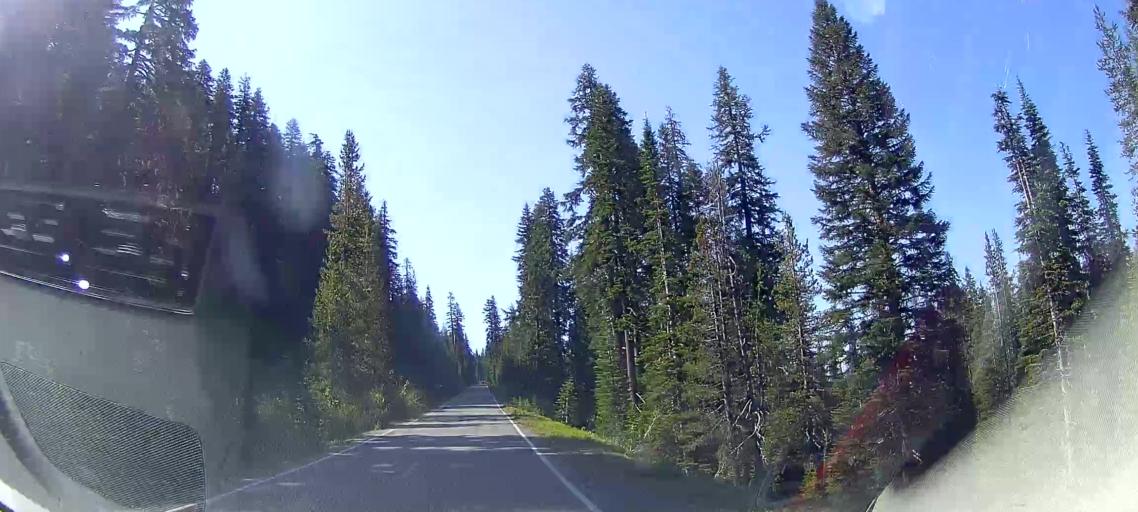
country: US
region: Oregon
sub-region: Jackson County
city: Shady Cove
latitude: 42.8892
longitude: -122.1317
